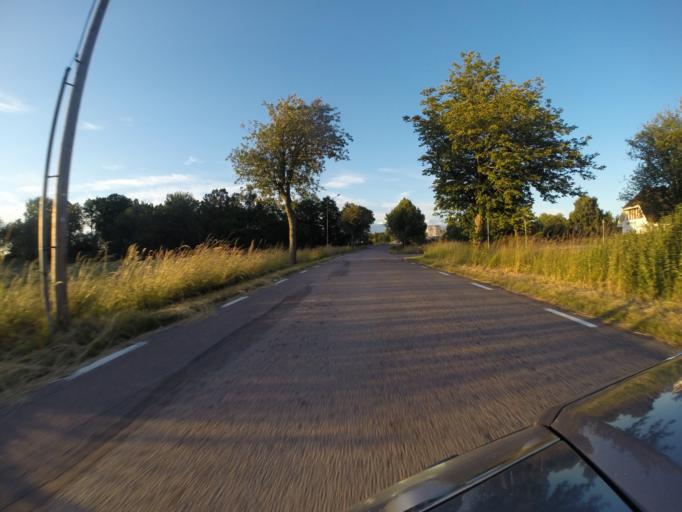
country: SE
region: Skane
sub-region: Bjuvs Kommun
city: Billesholm
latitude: 56.0501
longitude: 12.9627
